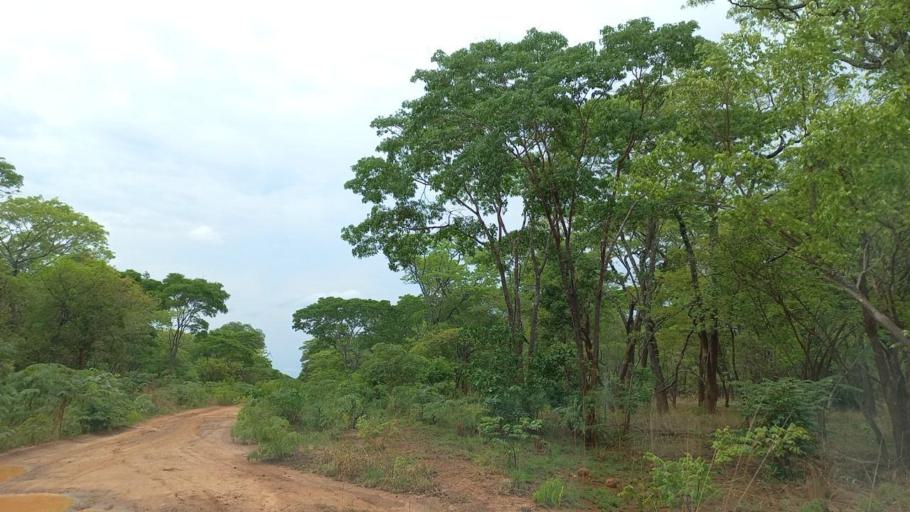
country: ZM
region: North-Western
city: Kalengwa
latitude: -13.6029
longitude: 24.9745
